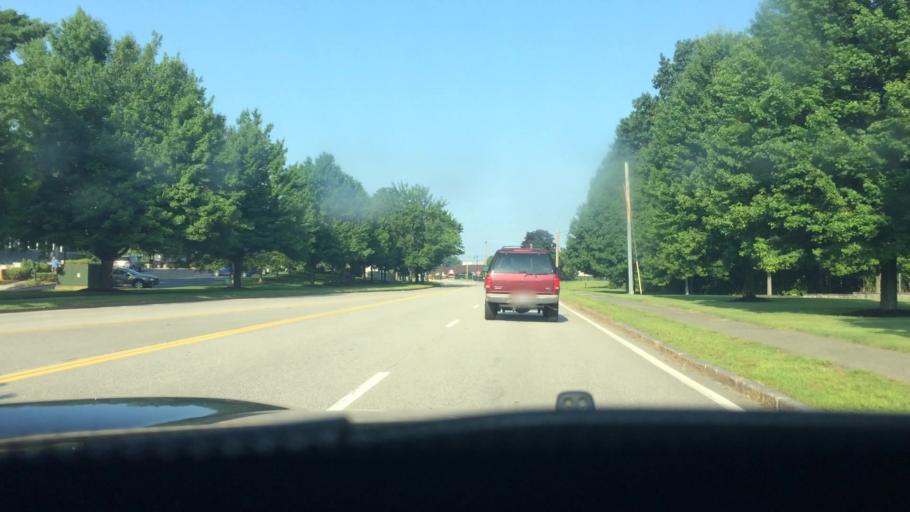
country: US
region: Maine
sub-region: York County
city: South Eliot
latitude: 43.0881
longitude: -70.8107
